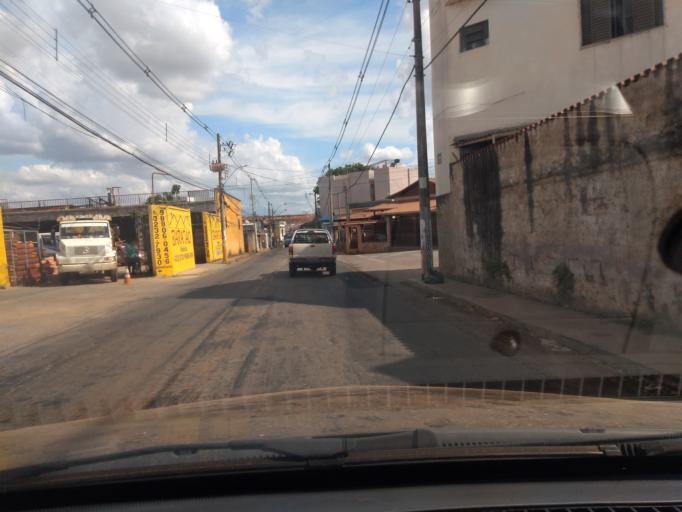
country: BR
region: Minas Gerais
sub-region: Tres Coracoes
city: Tres Coracoes
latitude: -21.7054
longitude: -45.2508
